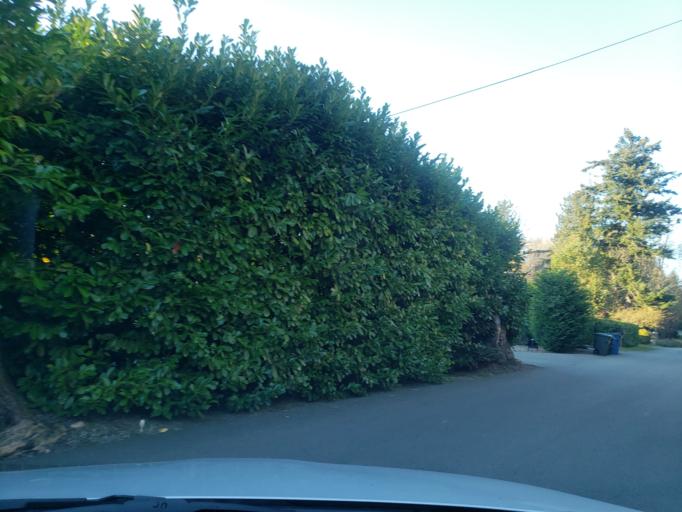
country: US
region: Washington
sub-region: Snohomish County
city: Woodway
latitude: 47.7798
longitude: -122.3855
